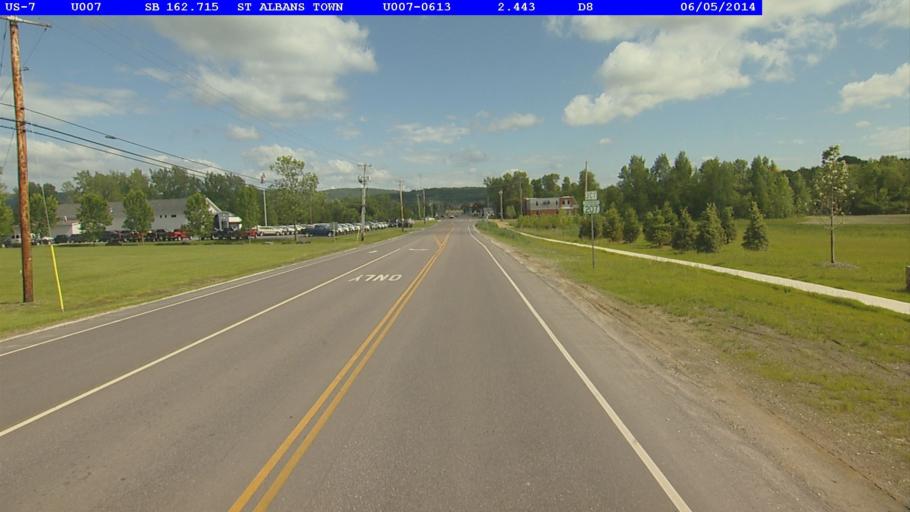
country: US
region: Vermont
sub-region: Franklin County
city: Saint Albans
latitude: 44.8430
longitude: -73.0850
